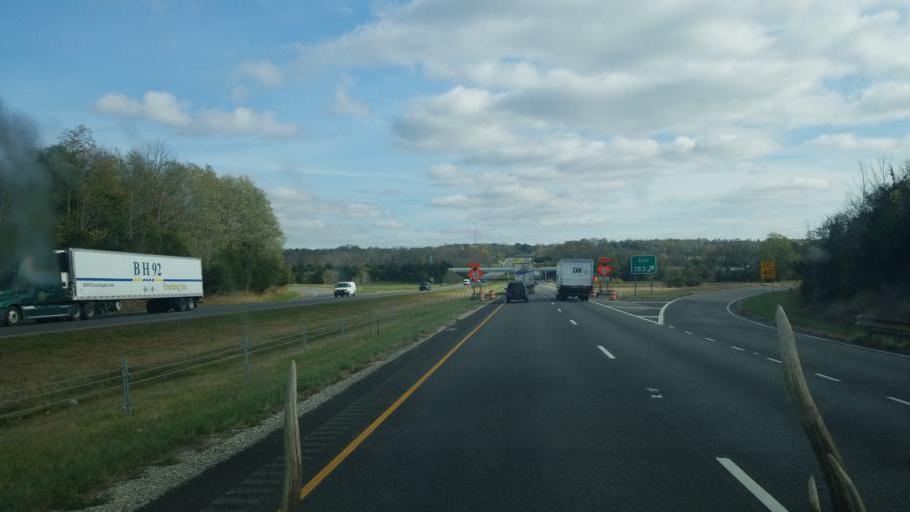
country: US
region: Indiana
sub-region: Wayne County
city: Richmond
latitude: 39.8693
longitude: -84.8648
